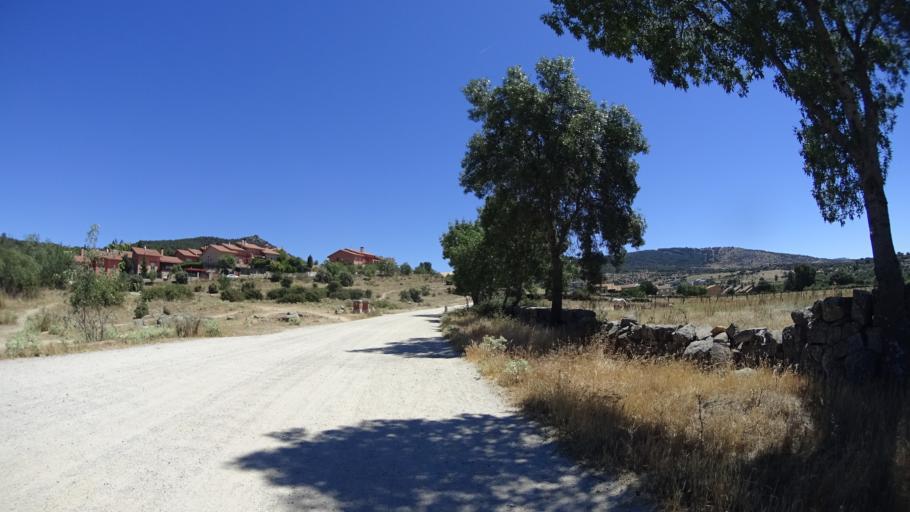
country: ES
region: Madrid
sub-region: Provincia de Madrid
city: Collado Mediano
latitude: 40.6882
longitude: -4.0320
